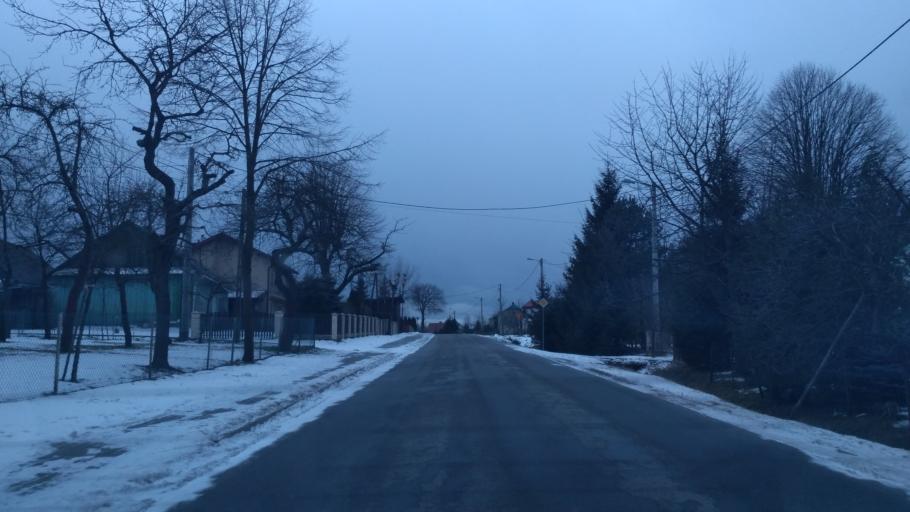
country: PL
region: Subcarpathian Voivodeship
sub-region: Powiat brzozowski
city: Wesola
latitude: 49.8358
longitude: 22.0894
